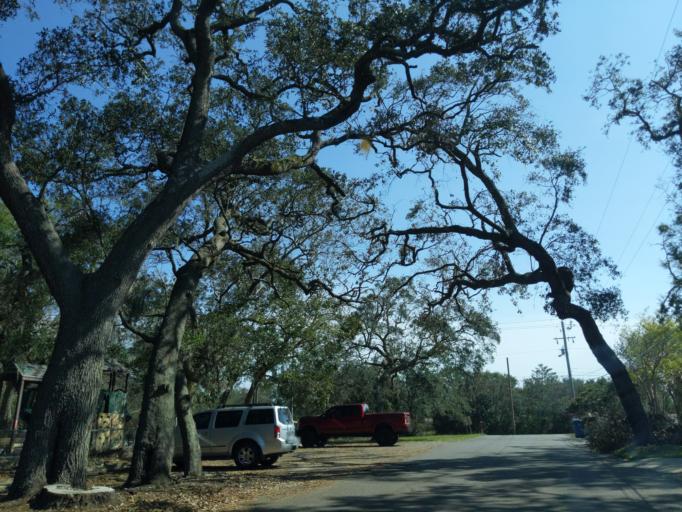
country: US
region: Florida
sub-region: Santa Rosa County
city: Gulf Breeze
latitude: 30.3615
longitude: -87.1809
